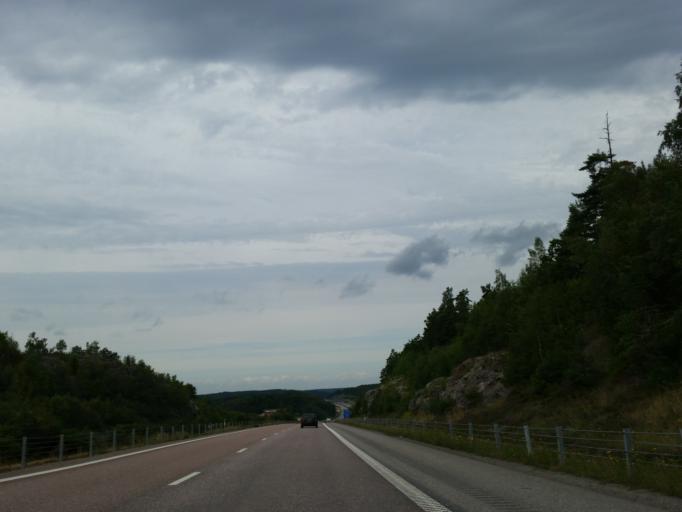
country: SE
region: Soedermanland
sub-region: Strangnas Kommun
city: Mariefred
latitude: 59.2359
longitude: 17.1882
